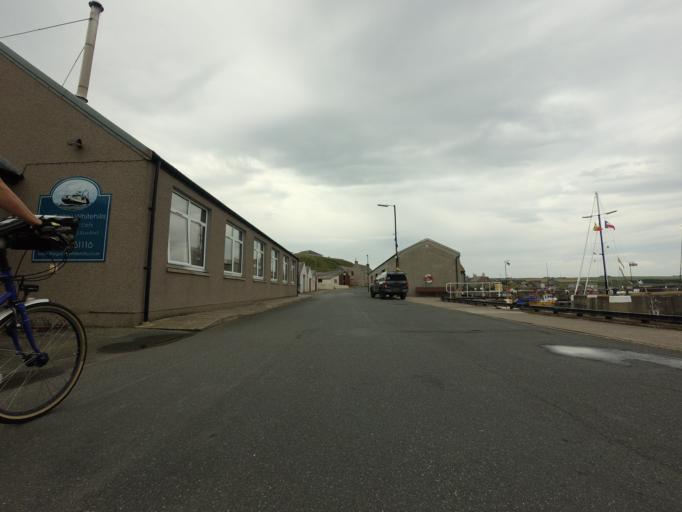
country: GB
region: Scotland
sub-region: Aberdeenshire
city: Whitehills
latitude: 57.6801
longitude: -2.5777
